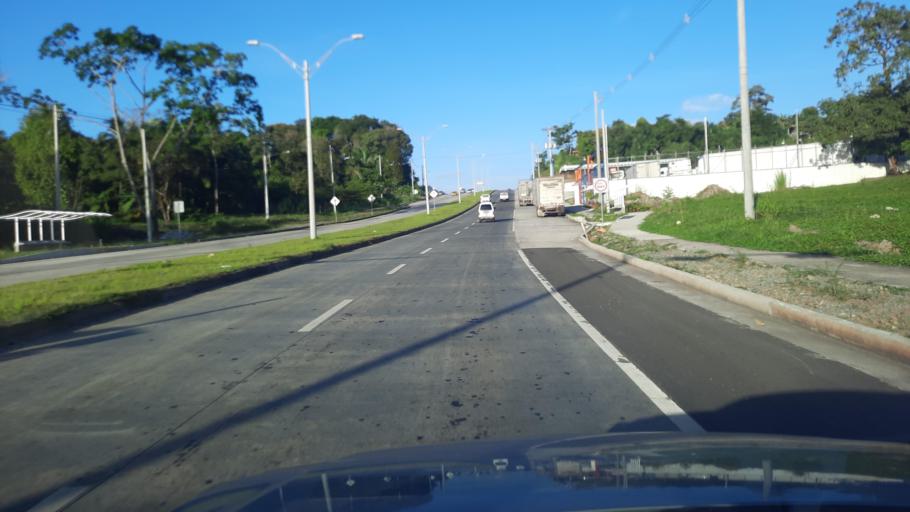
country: PA
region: Panama
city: Las Cumbres
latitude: 9.0985
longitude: -79.5085
